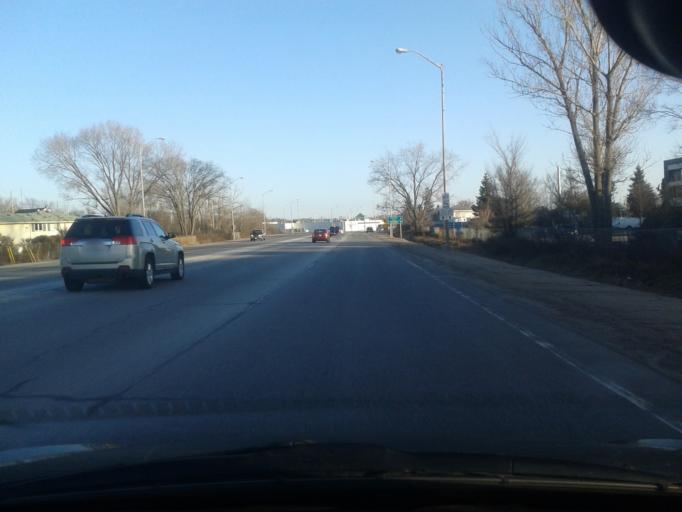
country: CA
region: Ontario
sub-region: Nipissing District
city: North Bay
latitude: 46.3209
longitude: -79.4453
